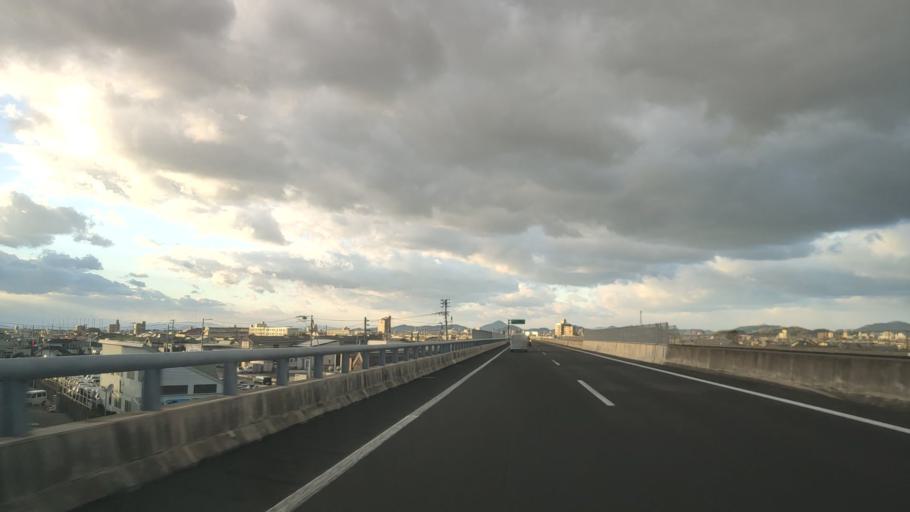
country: JP
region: Ehime
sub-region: Shikoku-chuo Shi
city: Matsuyama
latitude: 33.7906
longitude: 132.8043
